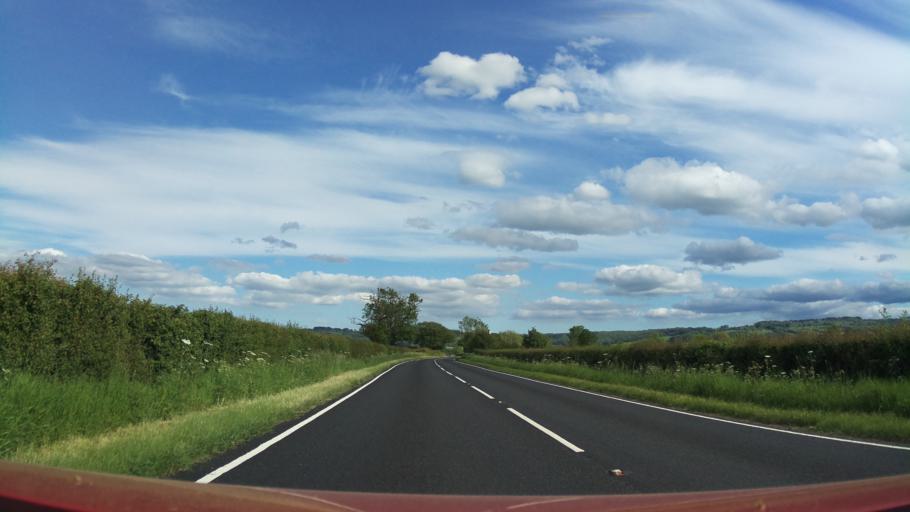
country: GB
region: England
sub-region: Worcestershire
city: Broadway
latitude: 52.0813
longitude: -1.8497
